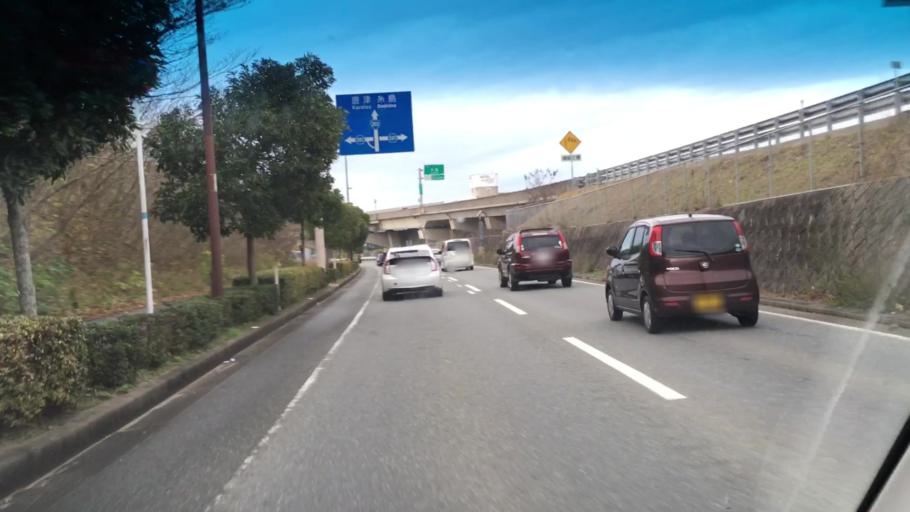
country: JP
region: Fukuoka
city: Maebaru-chuo
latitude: 33.5716
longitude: 130.2878
